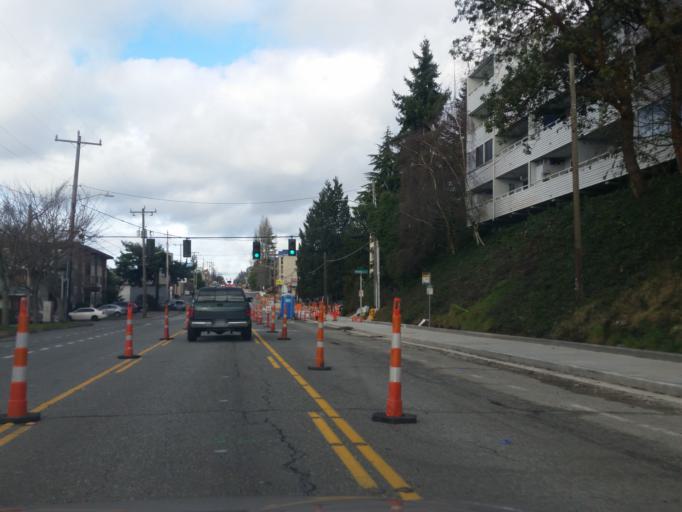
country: US
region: Washington
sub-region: King County
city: Shoreline
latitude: 47.6991
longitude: -122.3554
